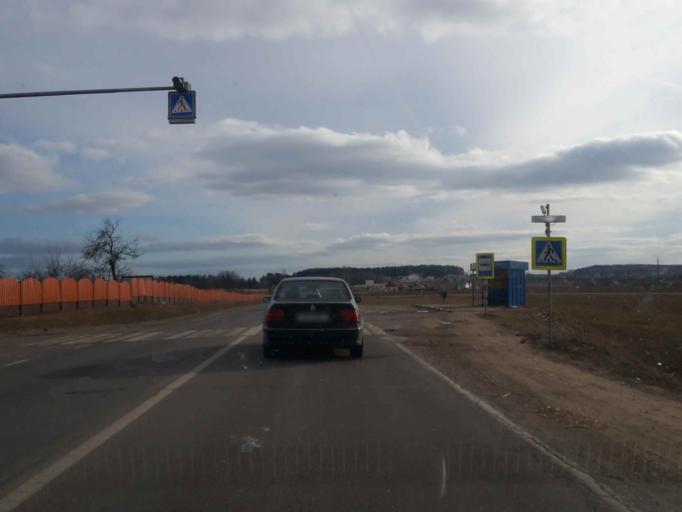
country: BY
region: Minsk
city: Bal'shavik
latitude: 54.0409
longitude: 27.5623
